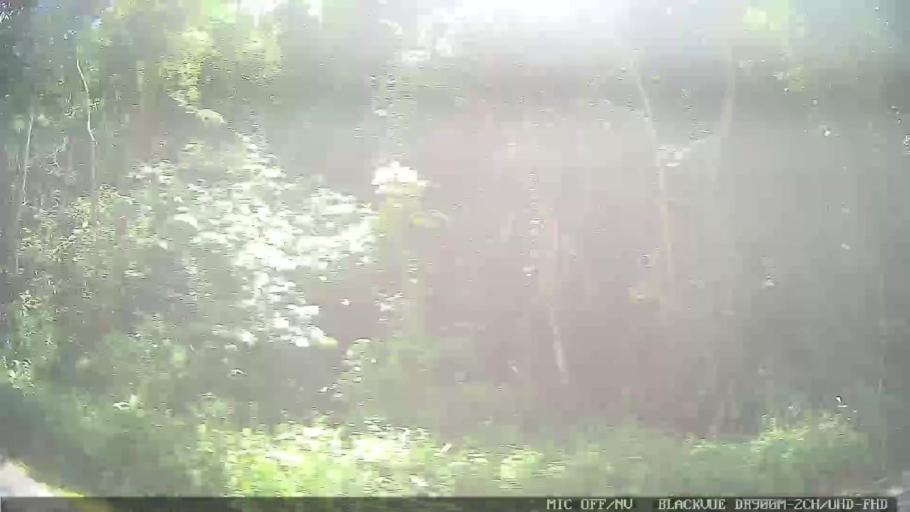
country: BR
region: Sao Paulo
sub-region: Amparo
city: Amparo
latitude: -22.7700
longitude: -46.7387
